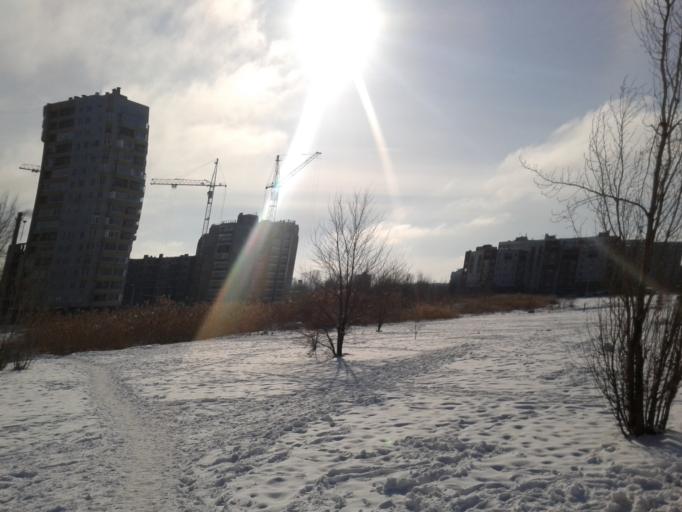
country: RU
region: Volgograd
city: Volgograd
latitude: 48.7474
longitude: 44.5003
